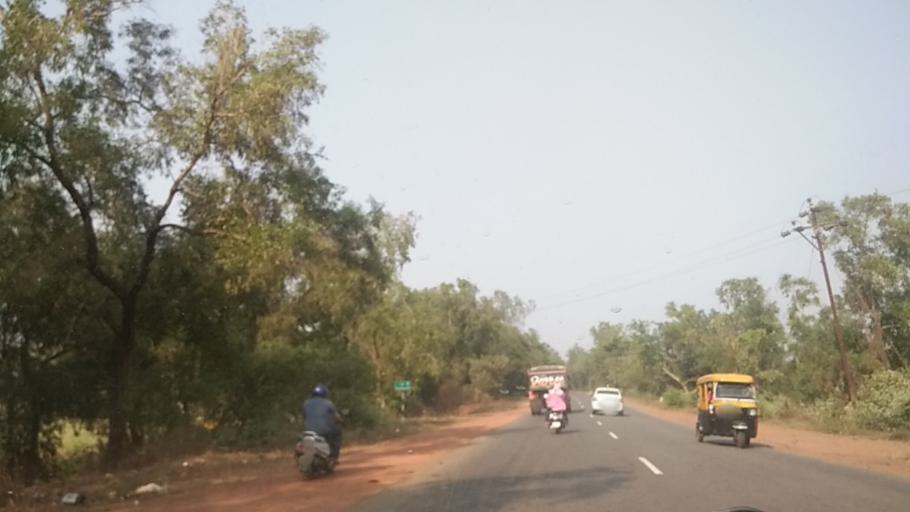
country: IN
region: Goa
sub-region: North Goa
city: Colovale
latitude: 15.6534
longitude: 73.8381
